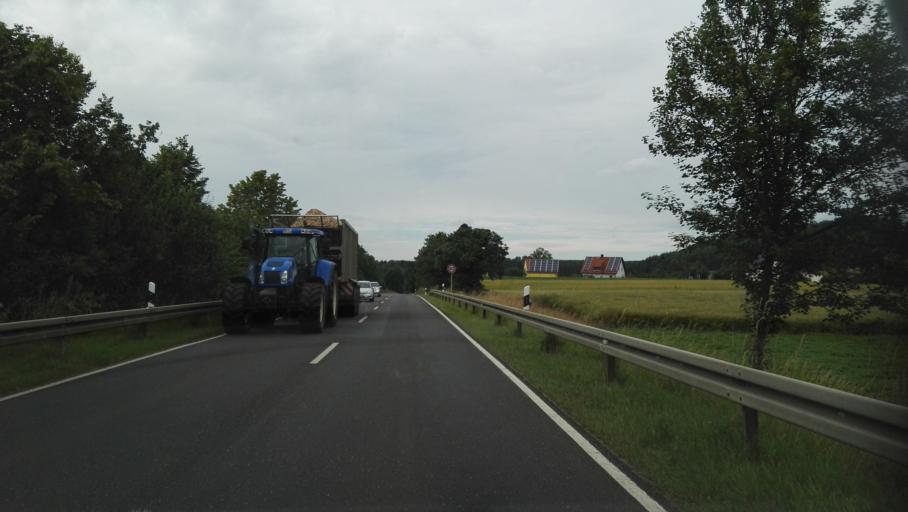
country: DE
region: Bavaria
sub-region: Upper Franconia
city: Plankenfels
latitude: 49.8928
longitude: 11.3346
